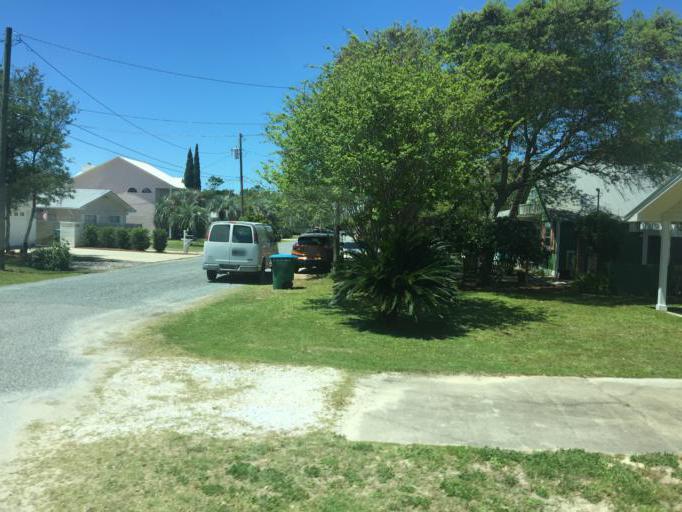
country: US
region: Florida
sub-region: Bay County
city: Laguna Beach
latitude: 30.2608
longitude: -85.9669
